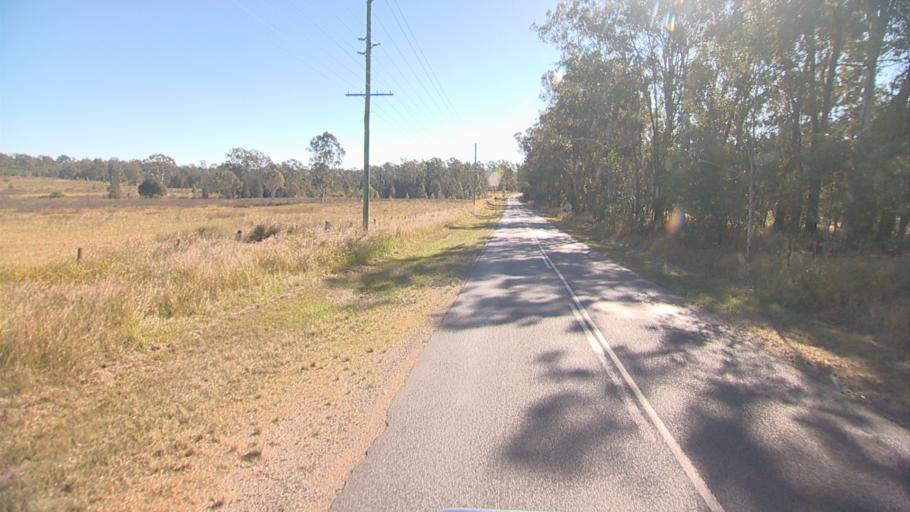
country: AU
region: Queensland
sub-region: Logan
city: North Maclean
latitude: -27.7670
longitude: 153.0005
